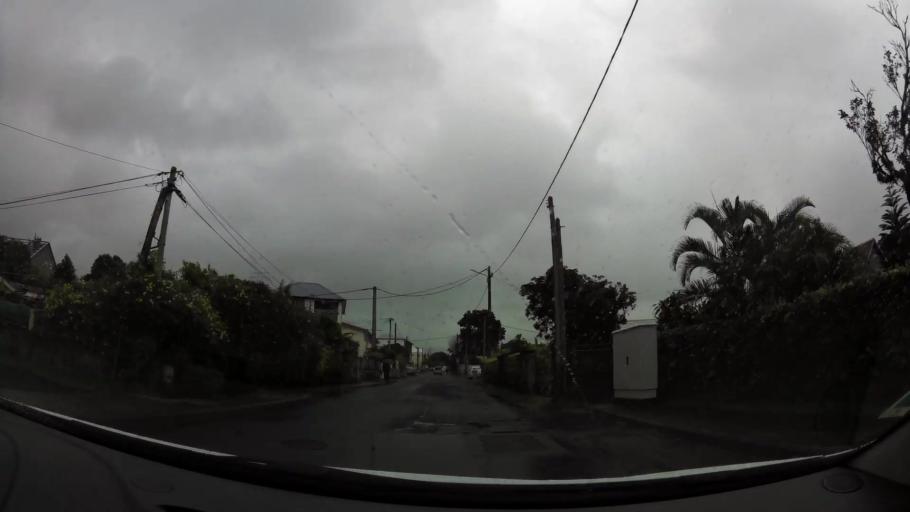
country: RE
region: Reunion
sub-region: Reunion
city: Saint-Andre
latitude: -20.9561
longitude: 55.6527
